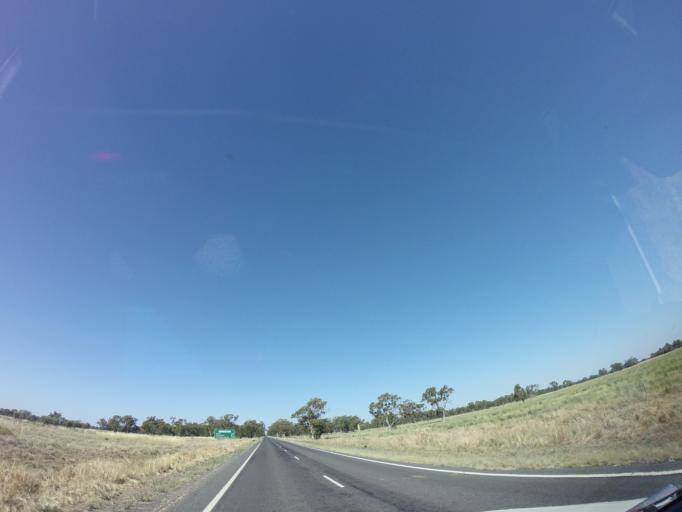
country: AU
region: New South Wales
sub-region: Narromine
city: Narromine
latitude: -31.6619
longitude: 147.8651
